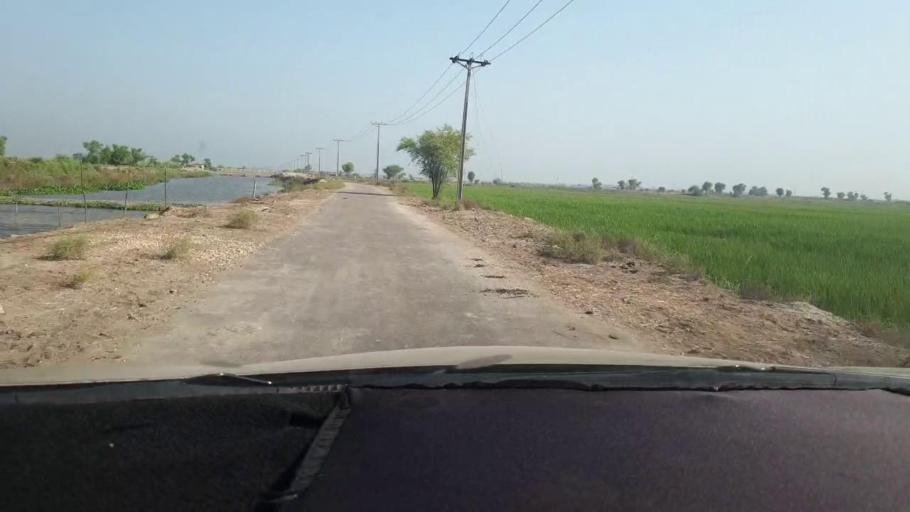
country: PK
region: Sindh
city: Miro Khan
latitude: 27.7612
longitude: 68.1336
